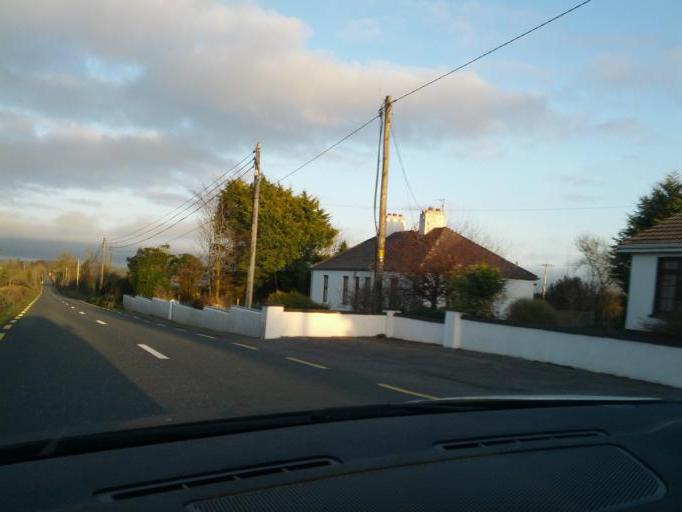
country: IE
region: Connaught
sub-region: Sligo
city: Tobercurry
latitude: 54.0441
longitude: -8.6683
